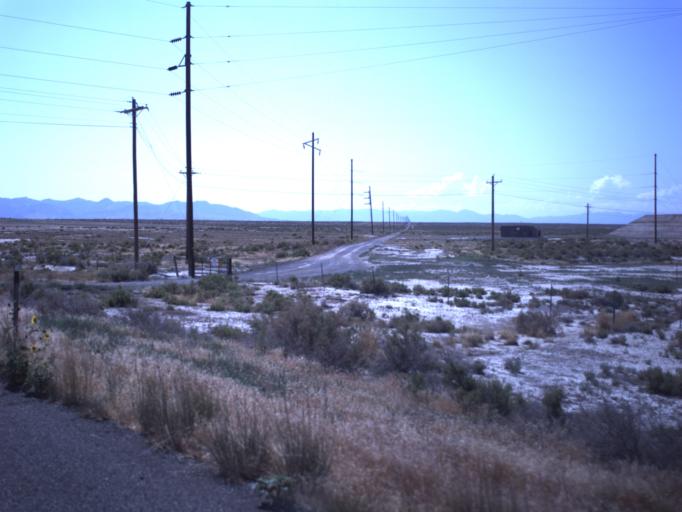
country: US
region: Utah
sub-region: Millard County
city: Delta
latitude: 39.4921
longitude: -112.5658
